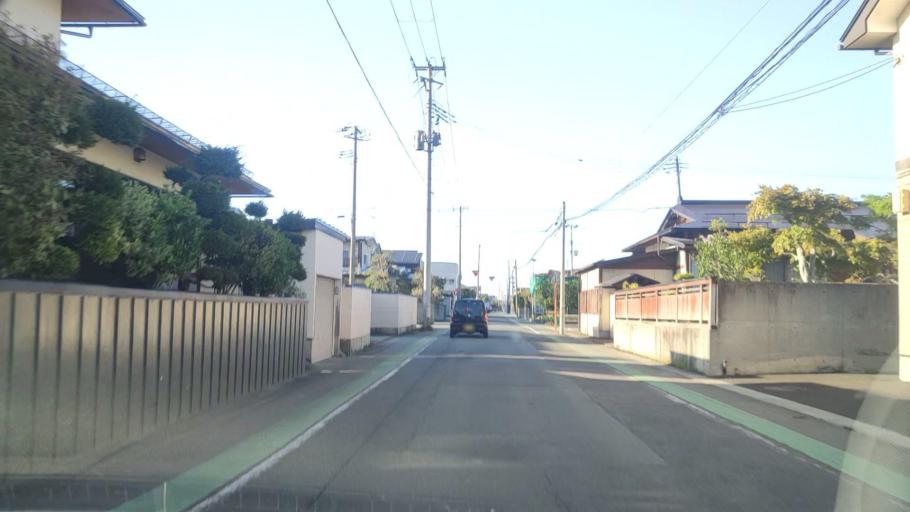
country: JP
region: Yamagata
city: Tendo
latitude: 38.3616
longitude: 140.3843
